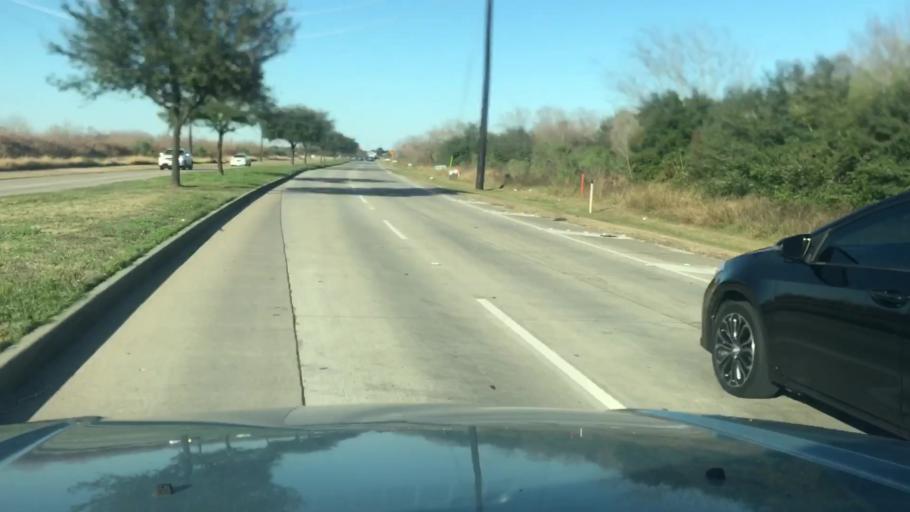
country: US
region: Texas
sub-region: Fort Bend County
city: Cinco Ranch
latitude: 29.8327
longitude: -95.7198
